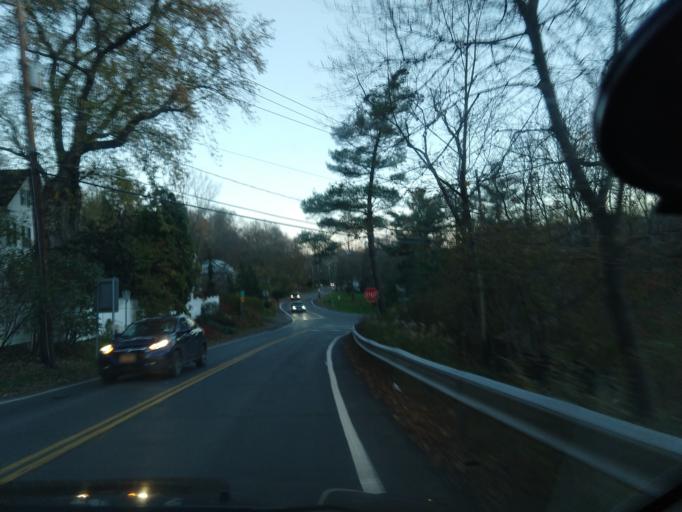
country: US
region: New York
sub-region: Tompkins County
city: East Ithaca
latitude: 42.4536
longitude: -76.4706
